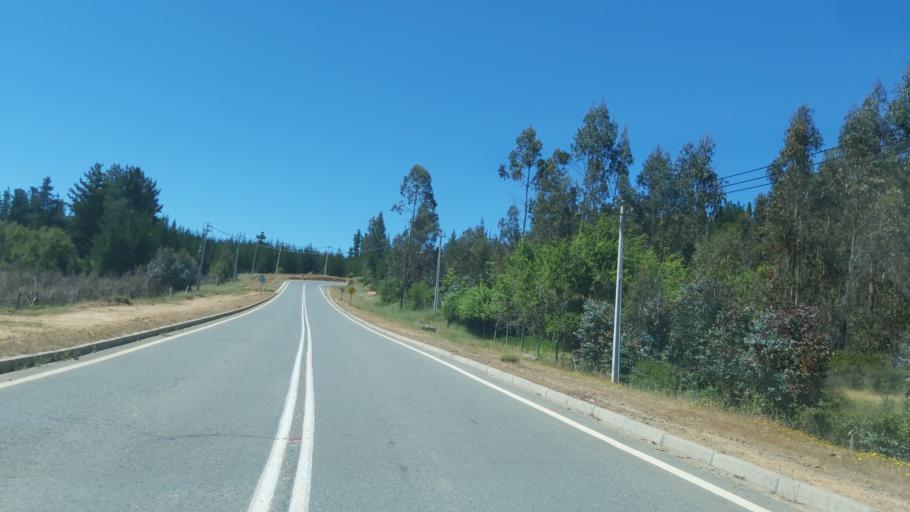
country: CL
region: Maule
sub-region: Provincia de Talca
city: Talca
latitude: -34.9565
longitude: -71.9616
